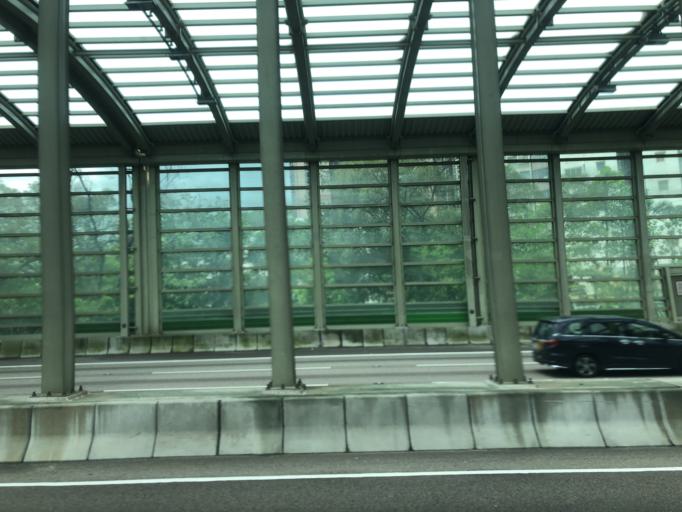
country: HK
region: Tsuen Wan
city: Tsuen Wan
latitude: 22.3677
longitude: 114.0642
